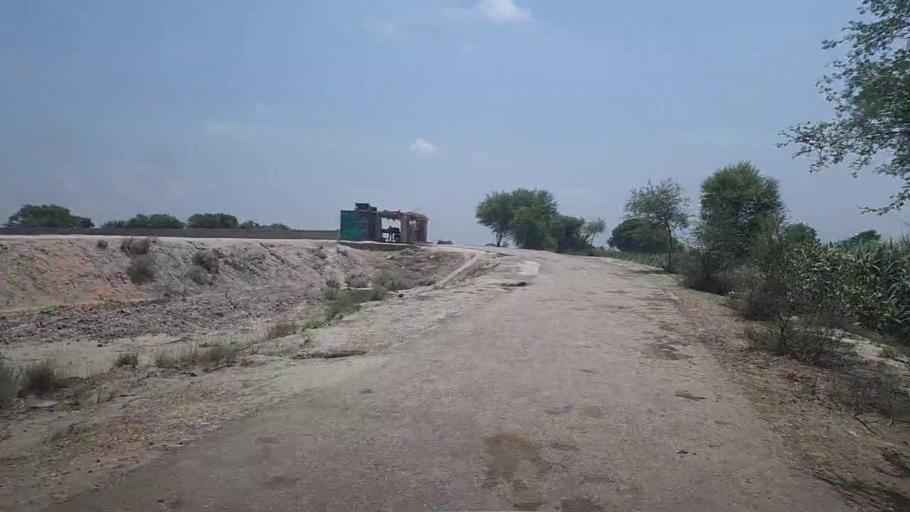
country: PK
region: Sindh
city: Ubauro
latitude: 28.2432
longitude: 69.8287
